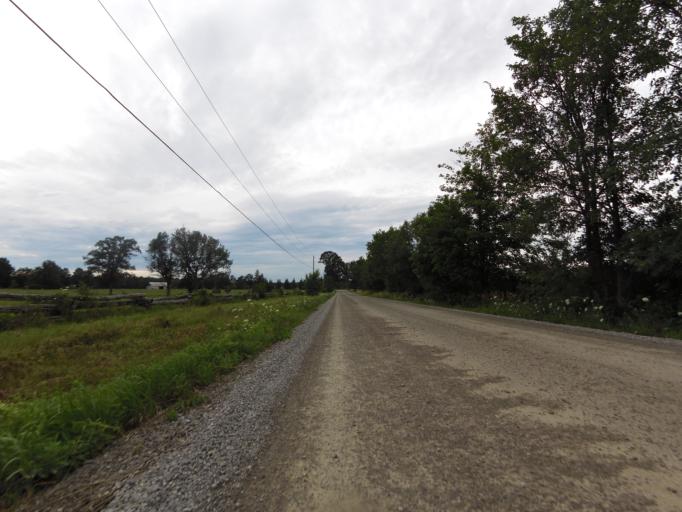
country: CA
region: Ontario
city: Carleton Place
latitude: 45.1483
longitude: -76.1752
